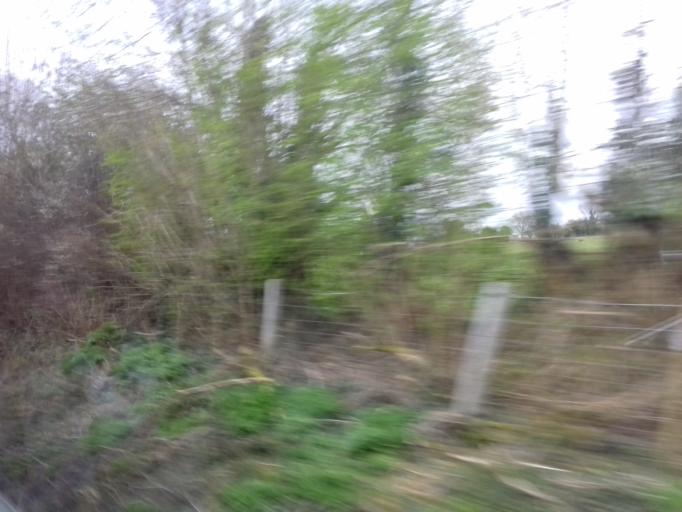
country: IE
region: Leinster
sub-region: An Longfort
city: Longford
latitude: 53.7555
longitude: -7.8267
